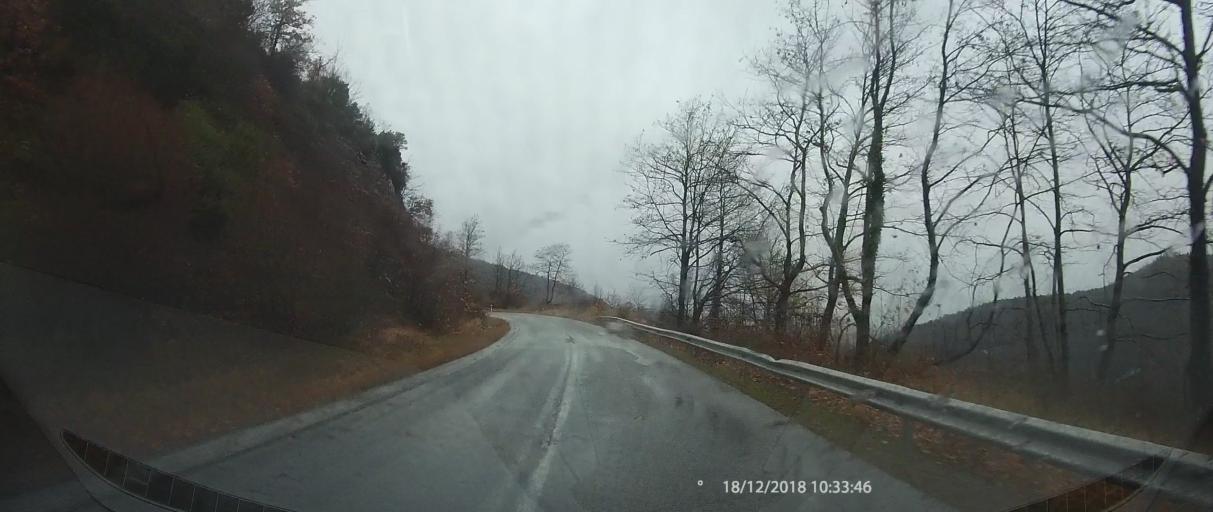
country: GR
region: Central Macedonia
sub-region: Nomos Pierias
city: Kato Milia
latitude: 40.2006
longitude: 22.3008
